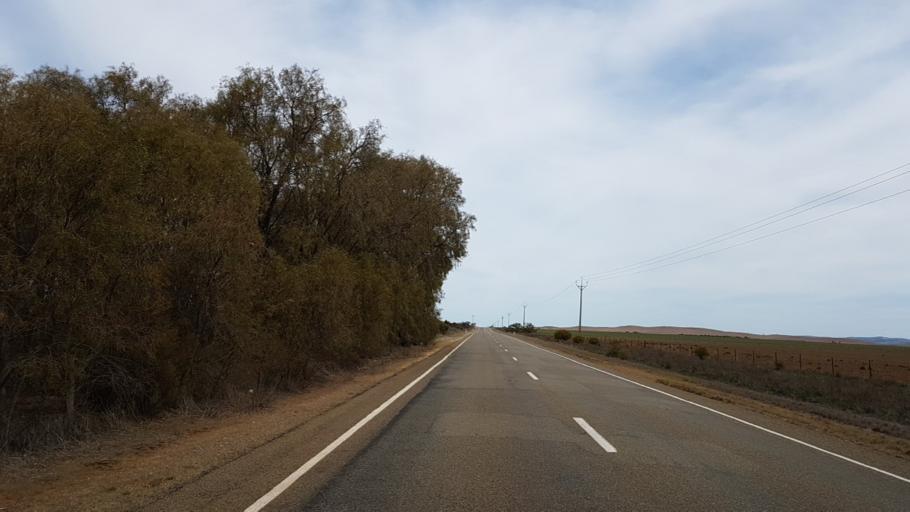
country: AU
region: South Australia
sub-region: Peterborough
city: Peterborough
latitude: -32.9978
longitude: 138.7815
